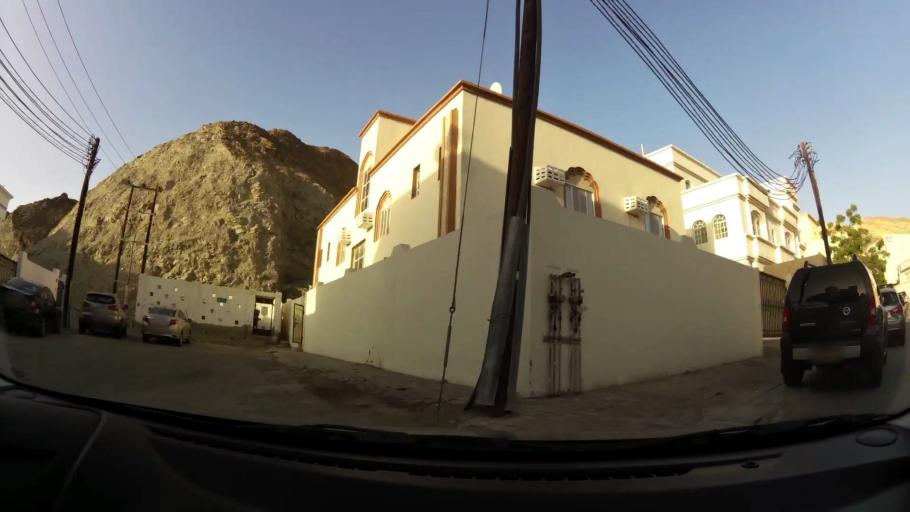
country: OM
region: Muhafazat Masqat
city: Muscat
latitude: 23.5650
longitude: 58.5829
